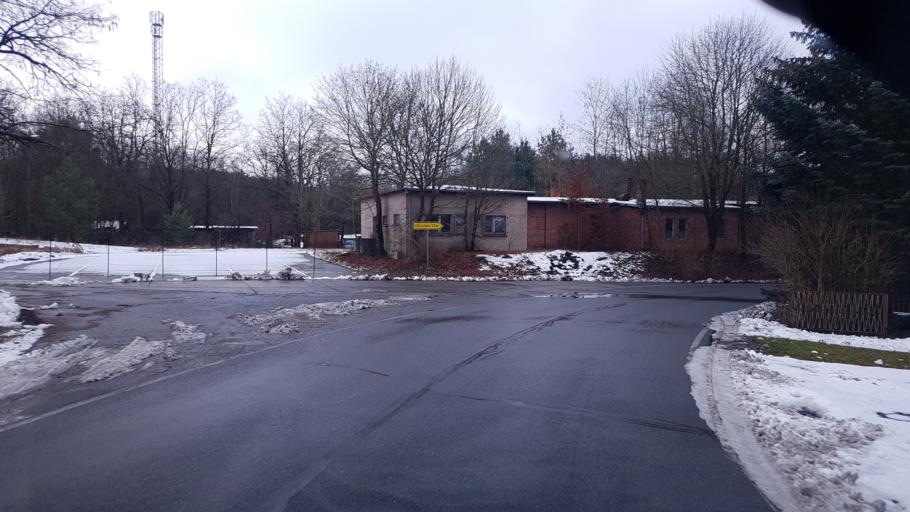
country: DE
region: Brandenburg
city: Jamlitz
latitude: 51.9899
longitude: 14.3707
